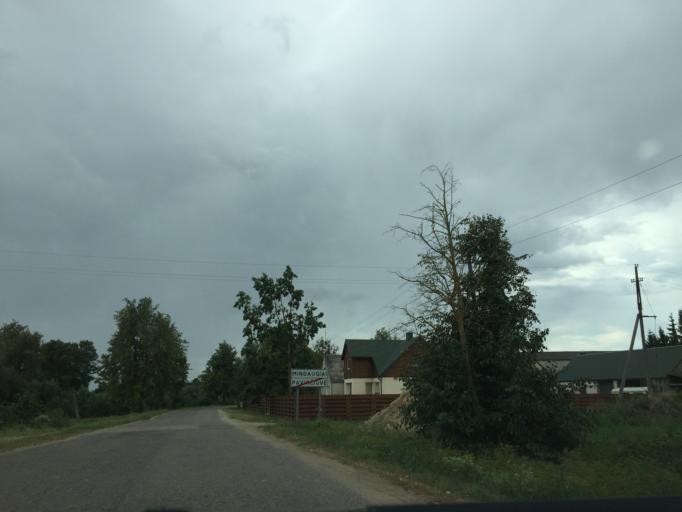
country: LT
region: Siauliu apskritis
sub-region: Joniskis
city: Joniskis
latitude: 56.2732
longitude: 23.7437
